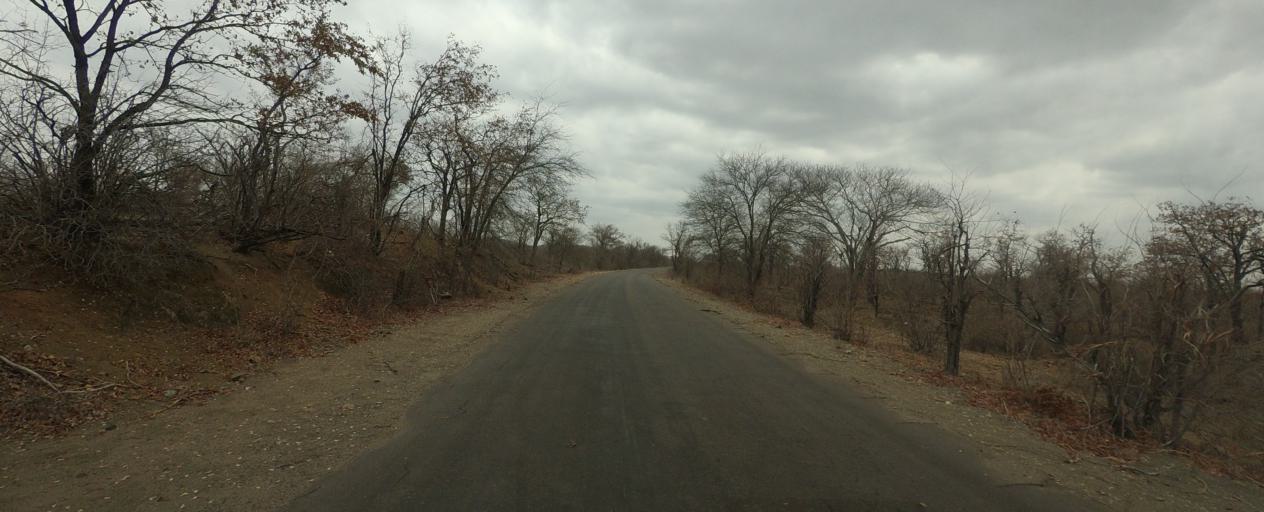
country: ZA
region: Limpopo
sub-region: Vhembe District Municipality
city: Mutale
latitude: -22.4000
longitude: 31.1947
